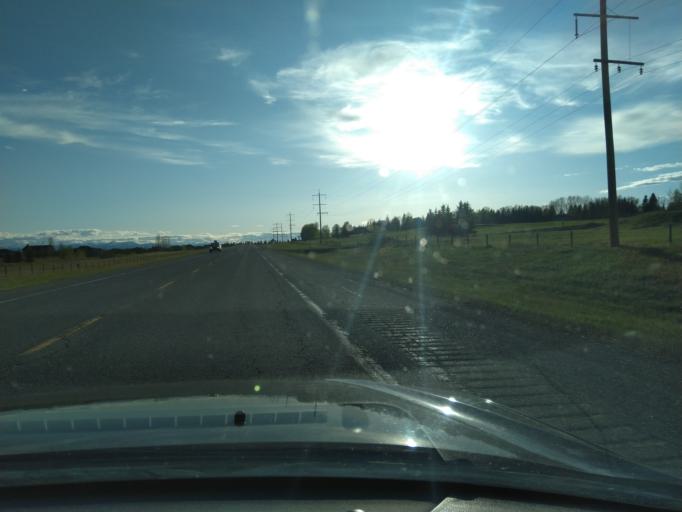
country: CA
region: Alberta
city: Cochrane
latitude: 51.0197
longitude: -114.3111
